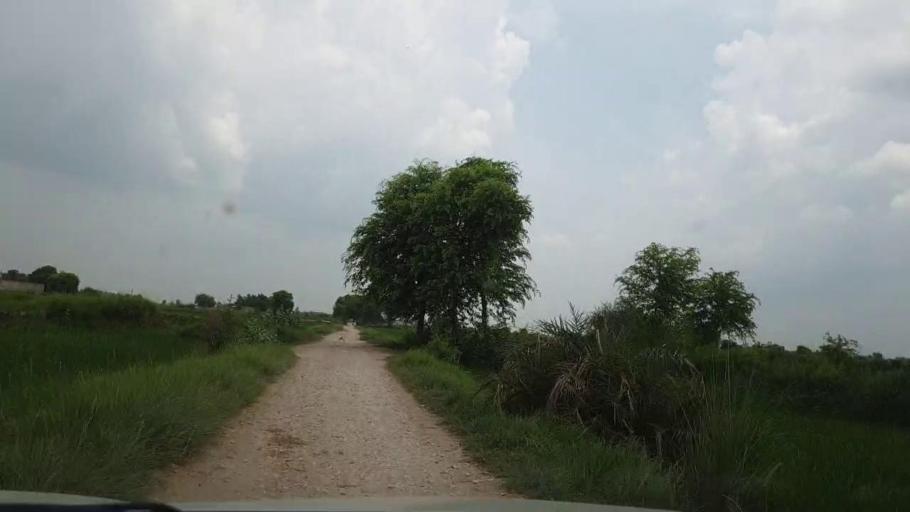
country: PK
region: Sindh
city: Goth Garelo
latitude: 27.4302
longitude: 68.0854
